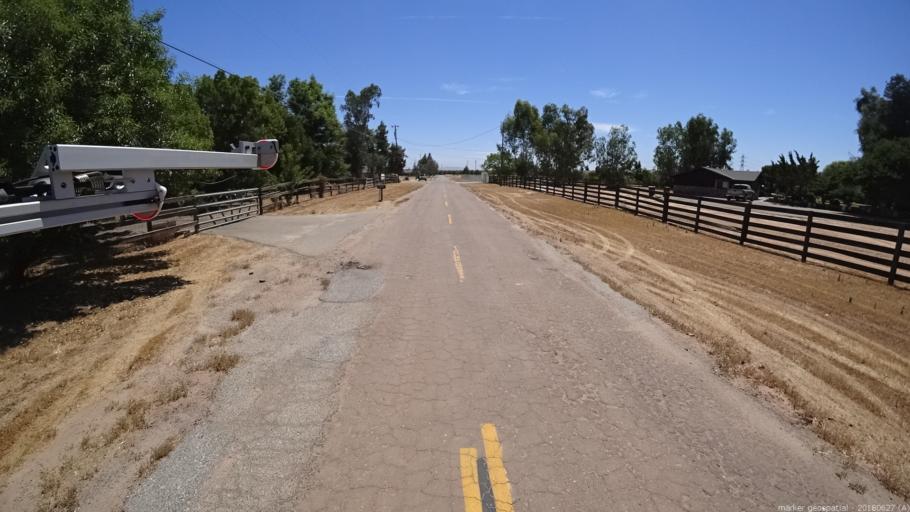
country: US
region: California
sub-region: Madera County
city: Bonadelle Ranchos-Madera Ranchos
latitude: 36.9358
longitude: -119.8622
